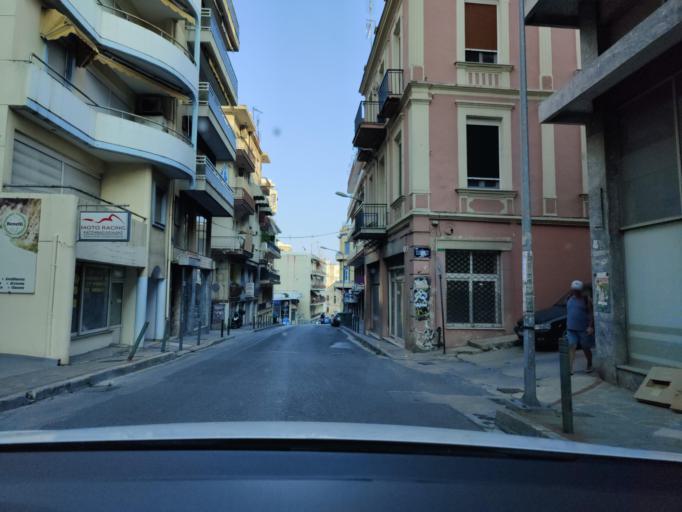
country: GR
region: East Macedonia and Thrace
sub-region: Nomos Kavalas
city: Kavala
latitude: 40.9390
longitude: 24.4051
